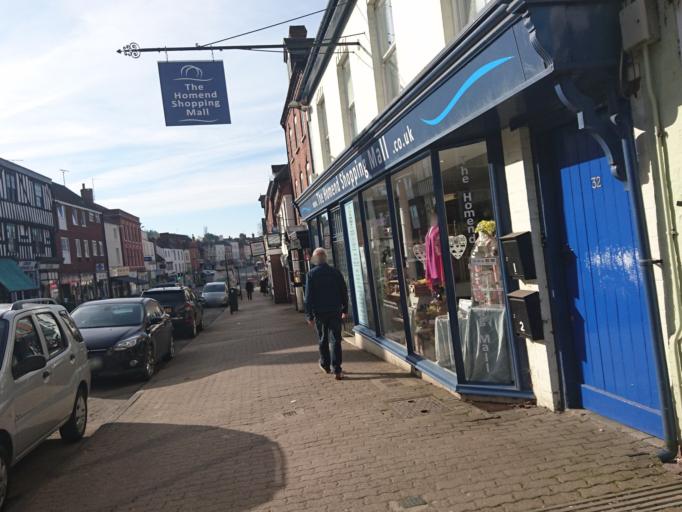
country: GB
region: England
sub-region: Herefordshire
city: Ledbury
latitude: 52.0383
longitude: -2.4239
